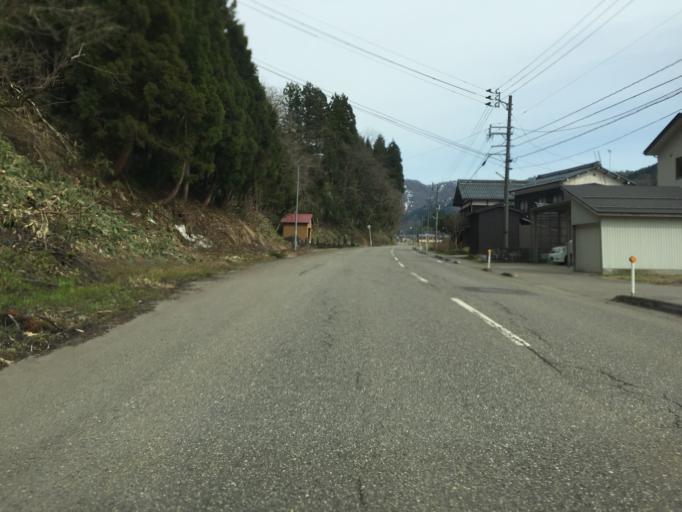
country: JP
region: Niigata
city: Tochio-honcho
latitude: 37.4473
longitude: 139.0203
